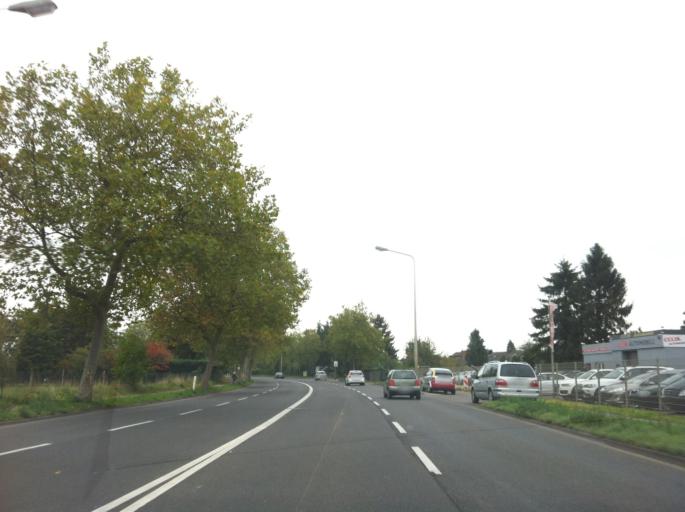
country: DE
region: North Rhine-Westphalia
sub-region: Regierungsbezirk Koln
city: Dueren
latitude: 50.7898
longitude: 6.5041
